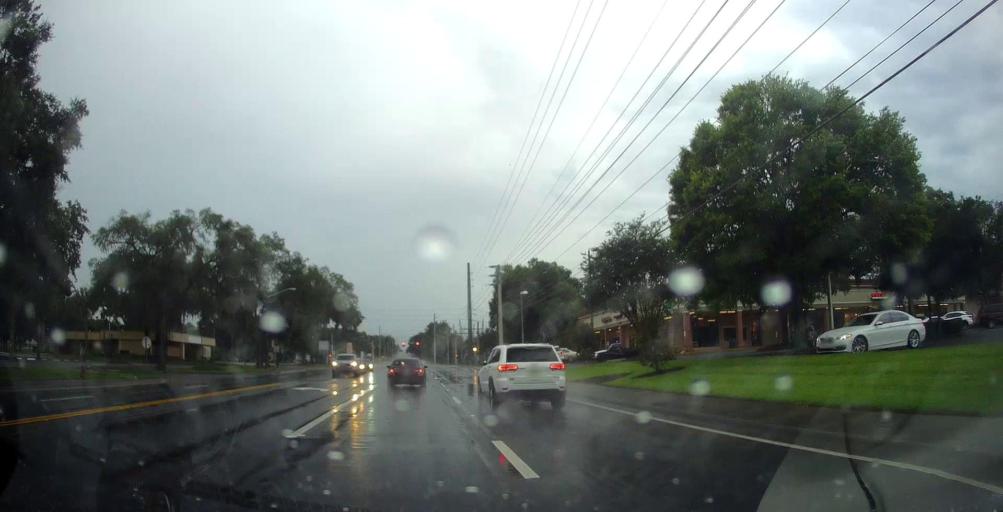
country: US
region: Florida
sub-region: Marion County
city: Ocala
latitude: 29.1952
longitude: -82.0869
